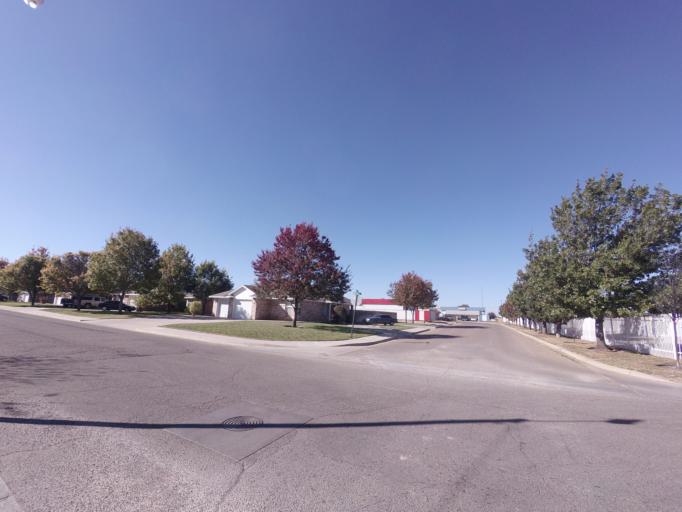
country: US
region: New Mexico
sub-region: Curry County
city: Clovis
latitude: 34.4318
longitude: -103.2002
